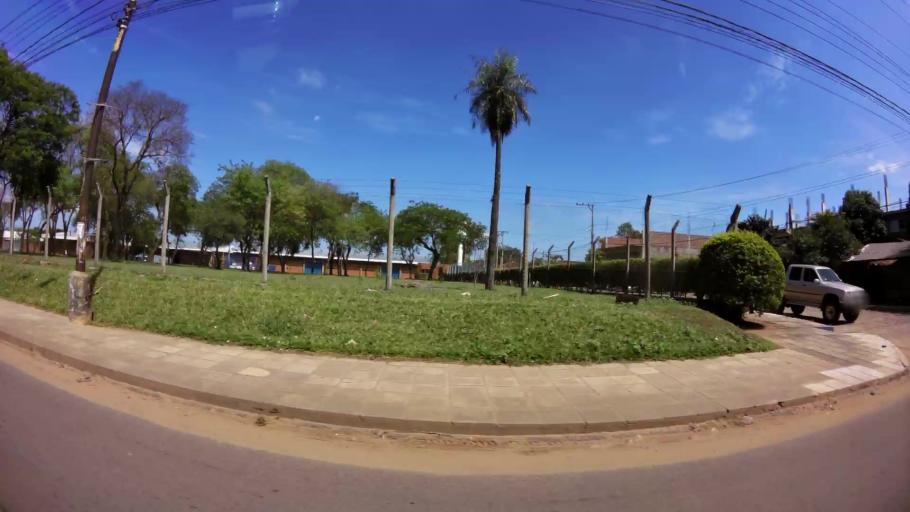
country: PY
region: Central
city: San Lorenzo
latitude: -25.2969
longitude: -57.5027
